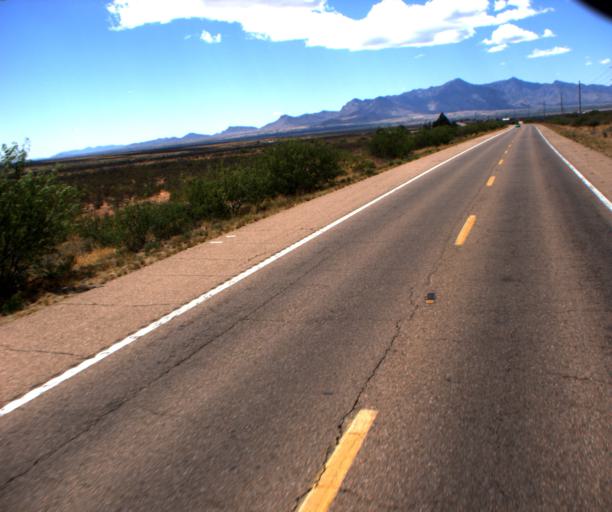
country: US
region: Arizona
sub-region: Cochise County
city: Naco
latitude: 31.3793
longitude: -110.0330
